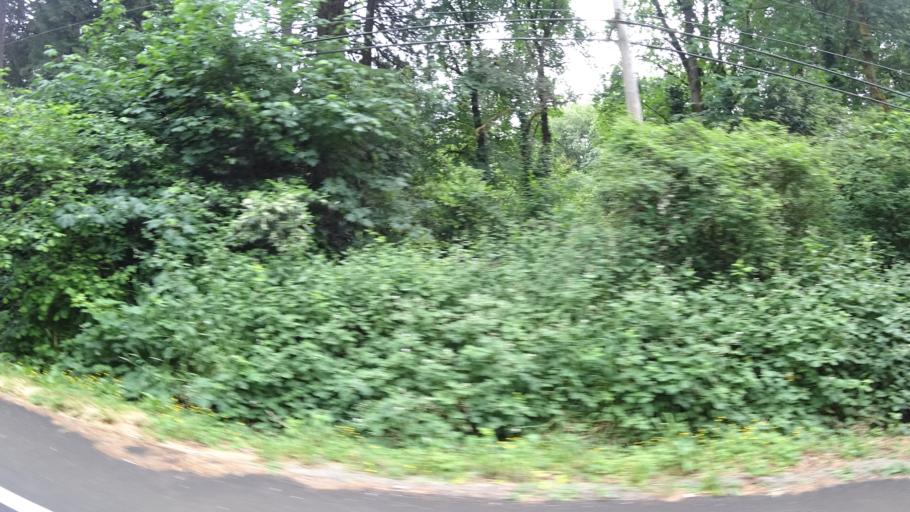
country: US
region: Oregon
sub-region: Clackamas County
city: Lake Oswego
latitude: 45.4327
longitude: -122.6663
